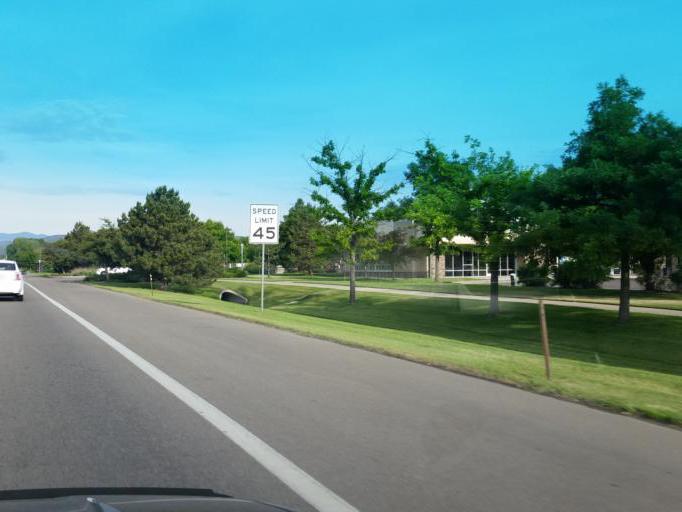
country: US
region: Colorado
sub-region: Larimer County
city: Fort Collins
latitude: 40.5238
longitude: -105.0495
